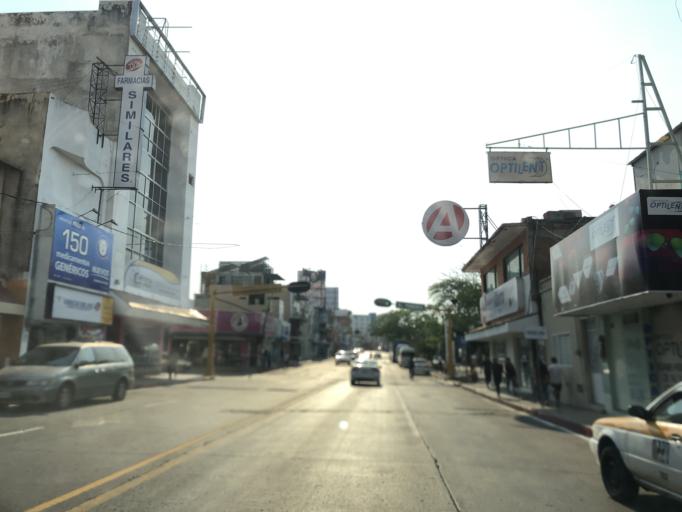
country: MX
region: Chiapas
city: Tuxtla Gutierrez
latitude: 16.7547
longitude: -93.1227
